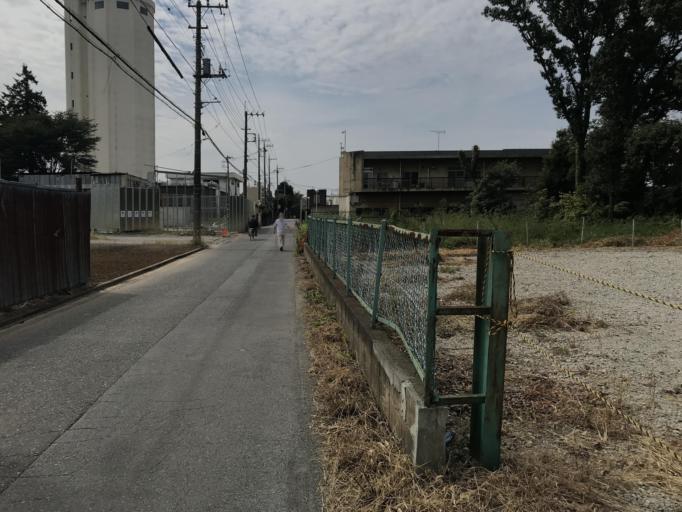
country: JP
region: Saitama
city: Asaka
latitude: 35.7804
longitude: 139.5567
